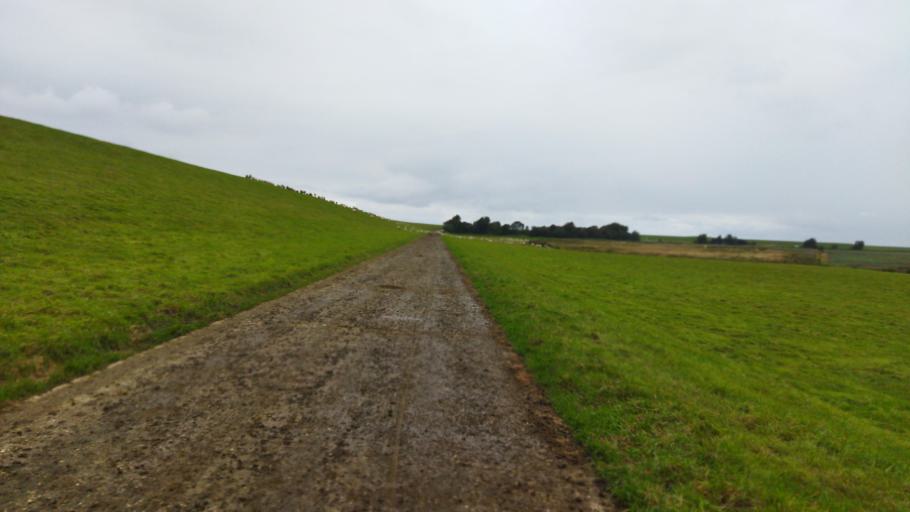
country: DE
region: Lower Saxony
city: Hinte
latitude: 53.4788
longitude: 7.0303
